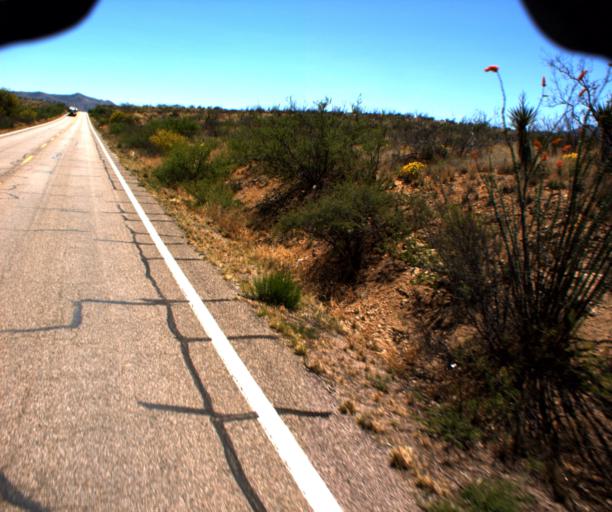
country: US
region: Arizona
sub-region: Pima County
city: Vail
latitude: 31.9789
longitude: -110.6785
